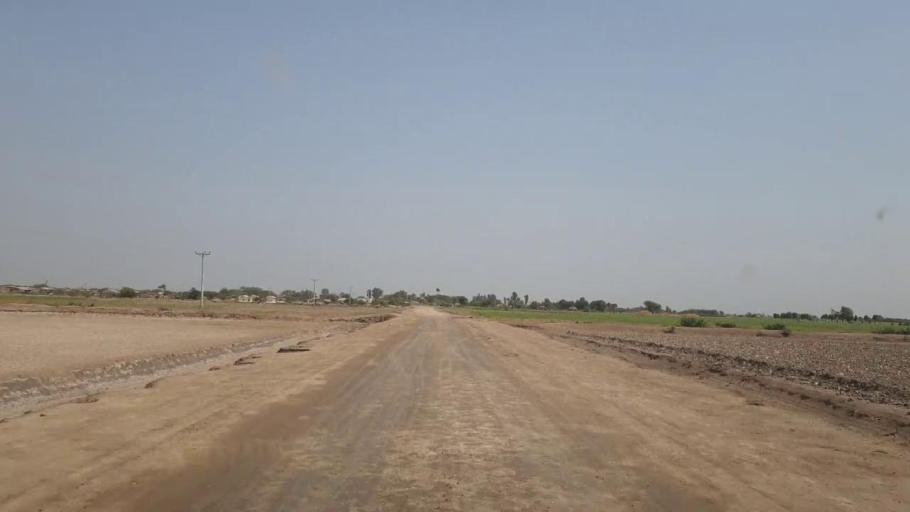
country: PK
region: Sindh
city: Jati
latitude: 24.4862
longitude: 68.5535
